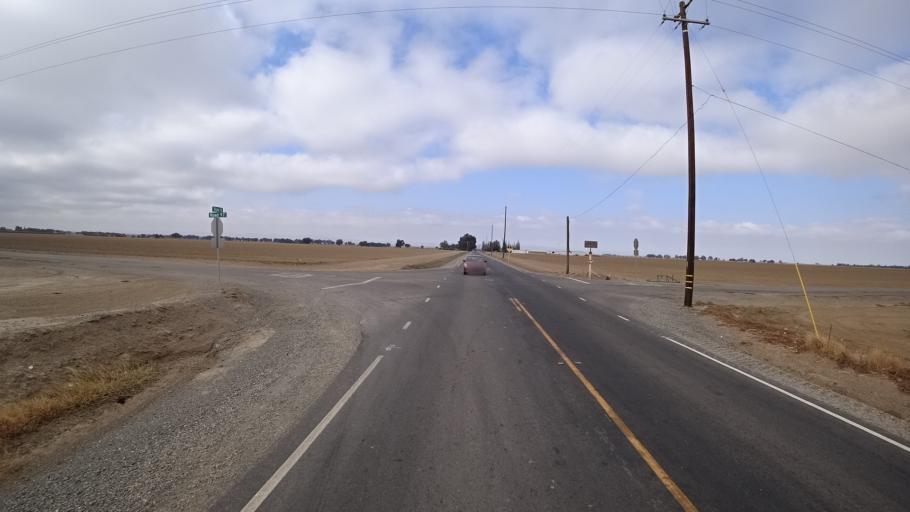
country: US
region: California
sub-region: Yolo County
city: Woodland
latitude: 38.7936
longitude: -121.8214
